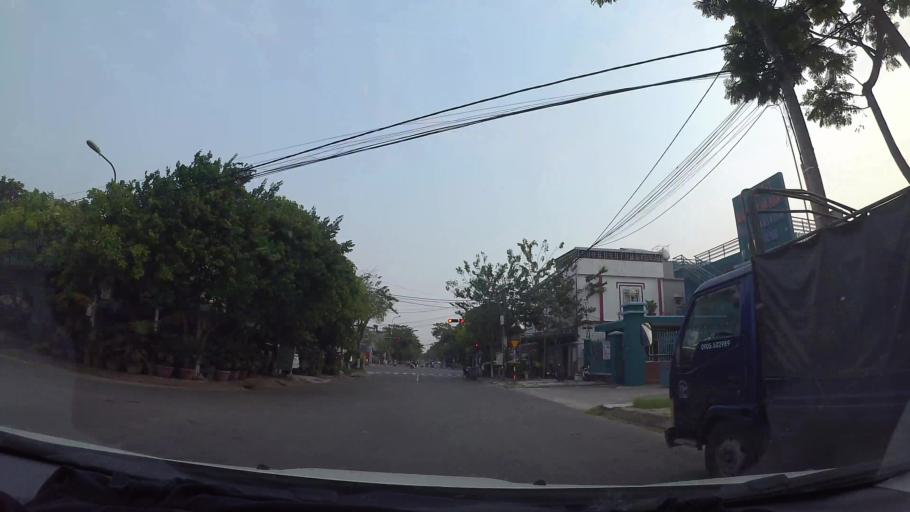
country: VN
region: Da Nang
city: Cam Le
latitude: 16.0232
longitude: 108.2019
